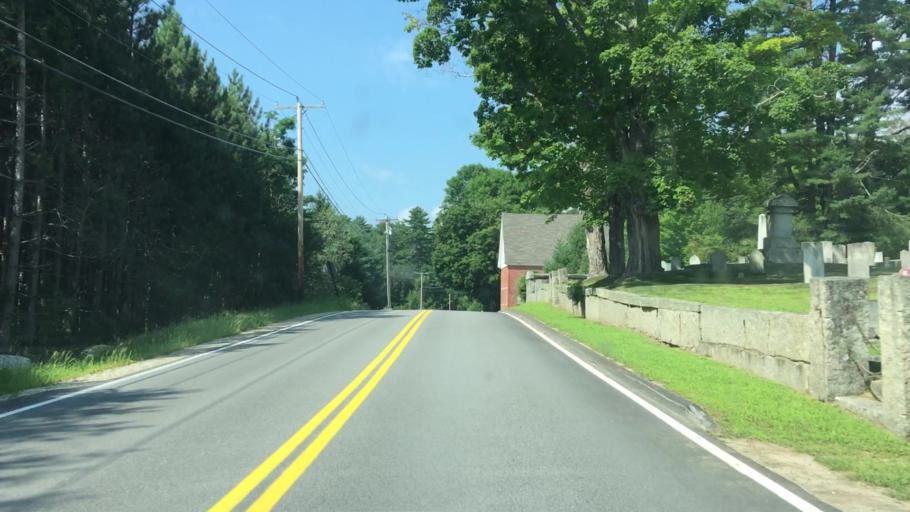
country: US
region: Maine
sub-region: Cumberland County
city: Raymond
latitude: 43.9017
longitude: -70.4626
